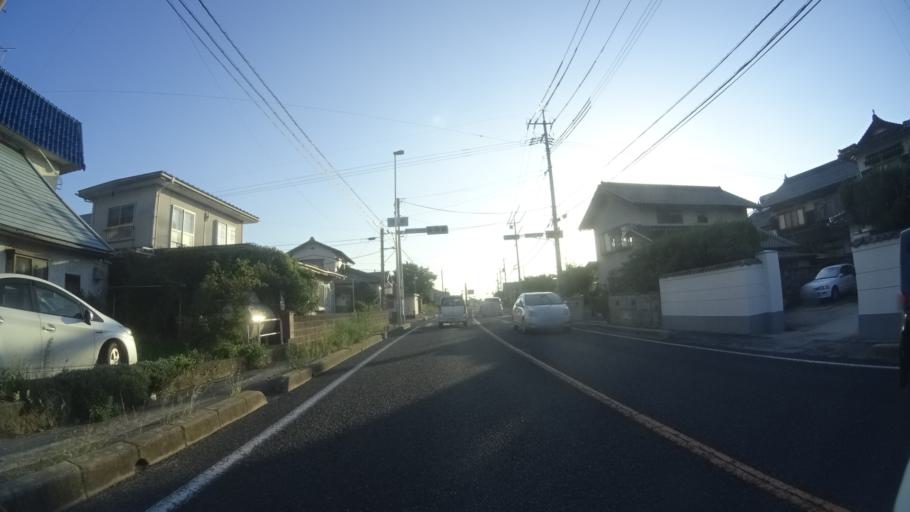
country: JP
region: Tottori
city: Yonago
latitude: 35.4544
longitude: 133.4218
